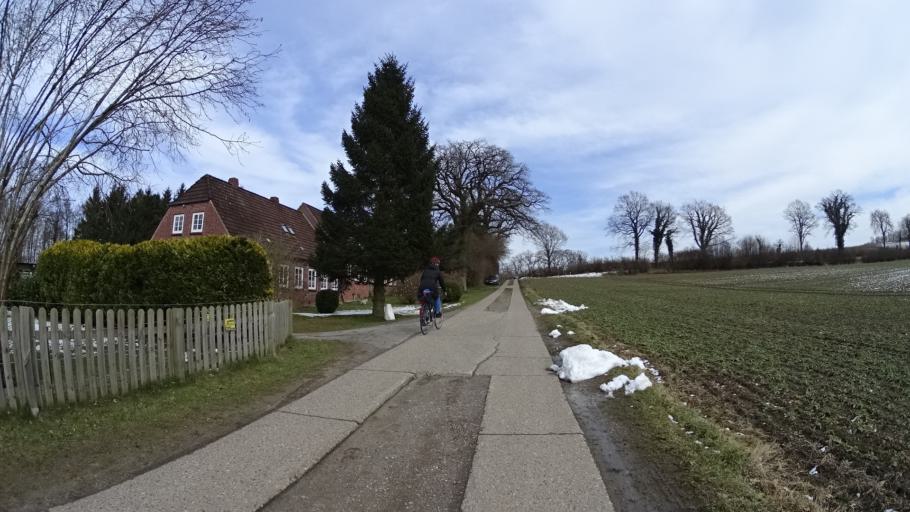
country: DE
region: Schleswig-Holstein
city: Kuhren
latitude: 54.1972
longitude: 10.2562
